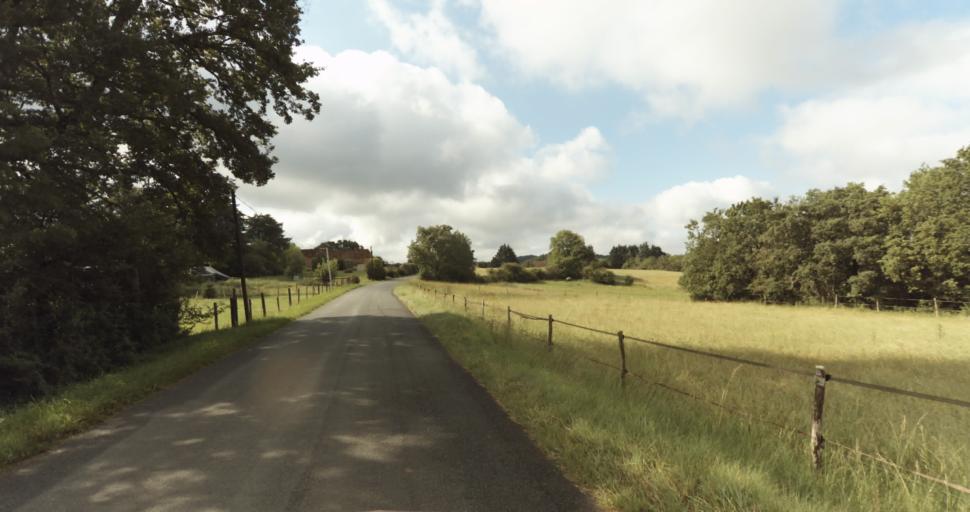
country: FR
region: Aquitaine
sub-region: Departement de la Dordogne
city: Le Bugue
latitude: 44.9263
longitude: 0.8217
